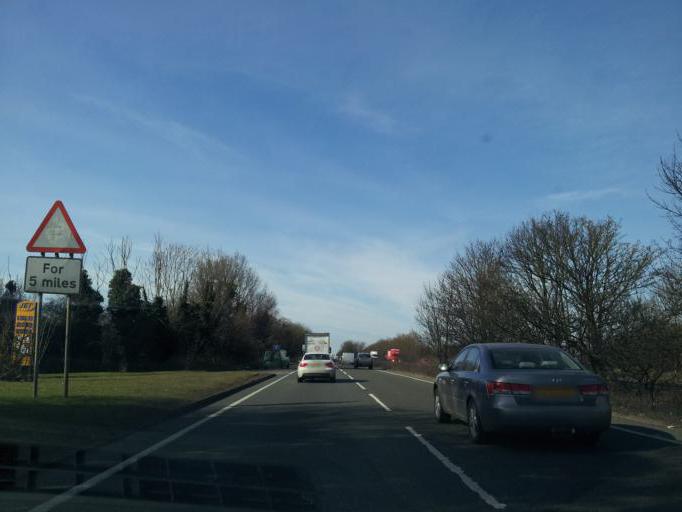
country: GB
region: England
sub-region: District of Rutland
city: Tickencote
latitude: 52.6744
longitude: -0.5326
